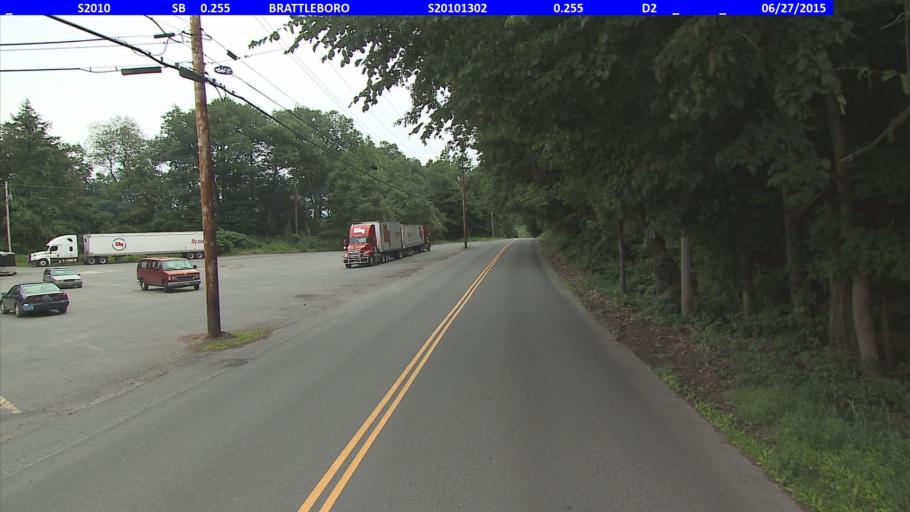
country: US
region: Vermont
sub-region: Windham County
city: Brattleboro
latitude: 42.8364
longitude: -72.5546
